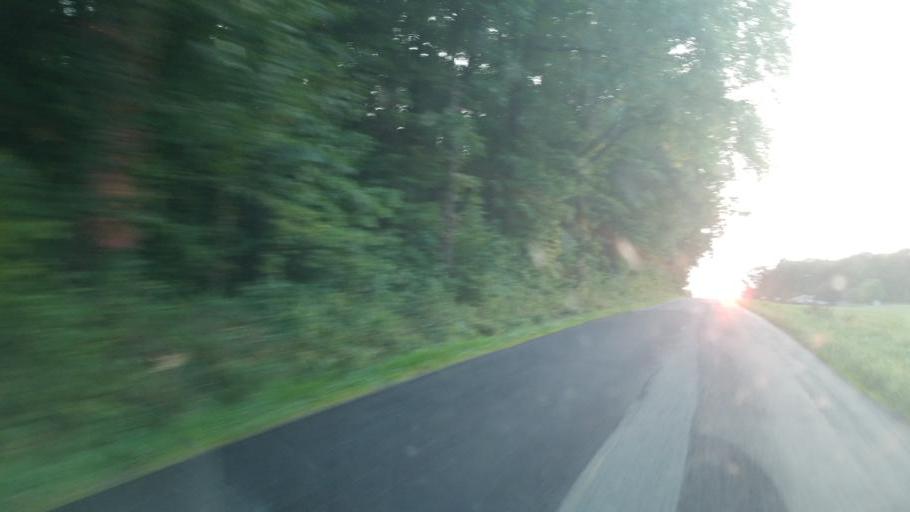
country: US
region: Ohio
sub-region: Knox County
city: Gambier
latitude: 40.4932
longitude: -82.3979
